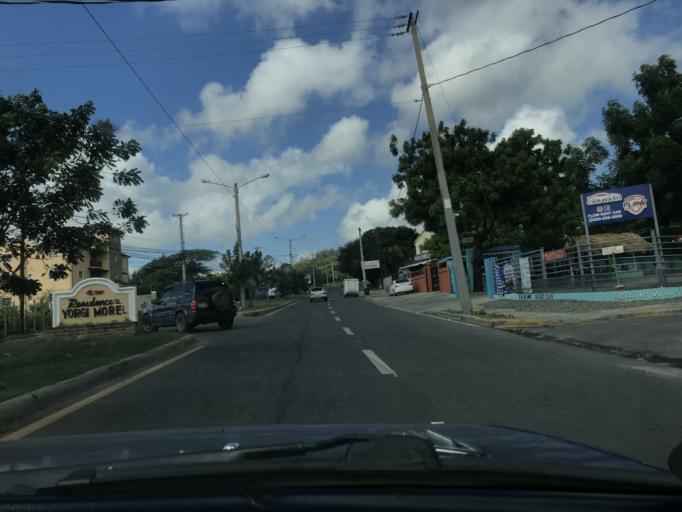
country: DO
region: Santiago
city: Santiago de los Caballeros
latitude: 19.4314
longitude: -70.7257
